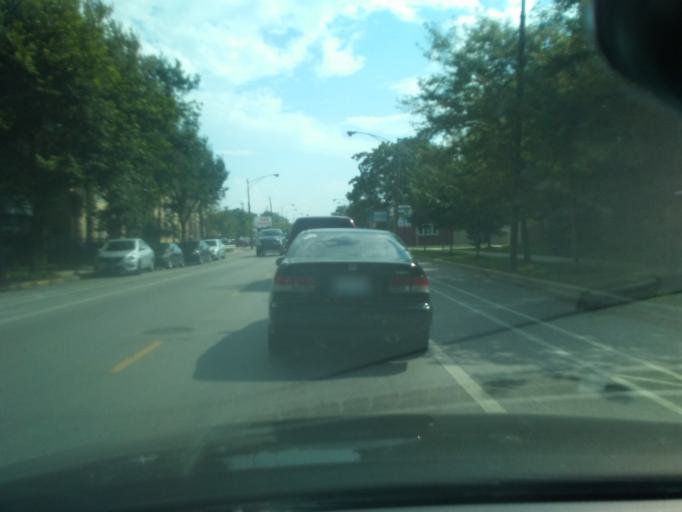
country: US
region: Illinois
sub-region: Cook County
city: Harwood Heights
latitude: 41.9693
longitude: -87.7675
